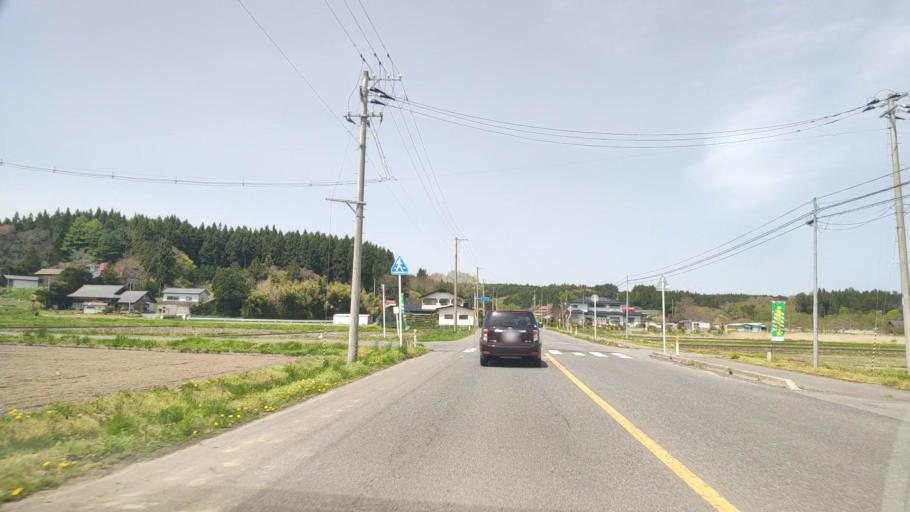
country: JP
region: Aomori
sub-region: Misawa Shi
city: Inuotose
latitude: 40.5594
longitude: 141.3858
